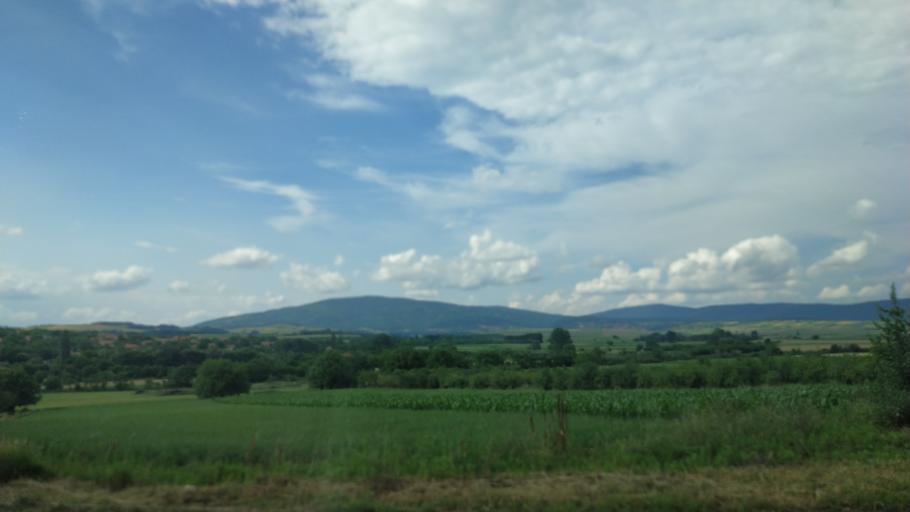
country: RS
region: Central Serbia
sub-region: Nisavski Okrug
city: Aleksinac
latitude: 43.6103
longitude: 21.6505
